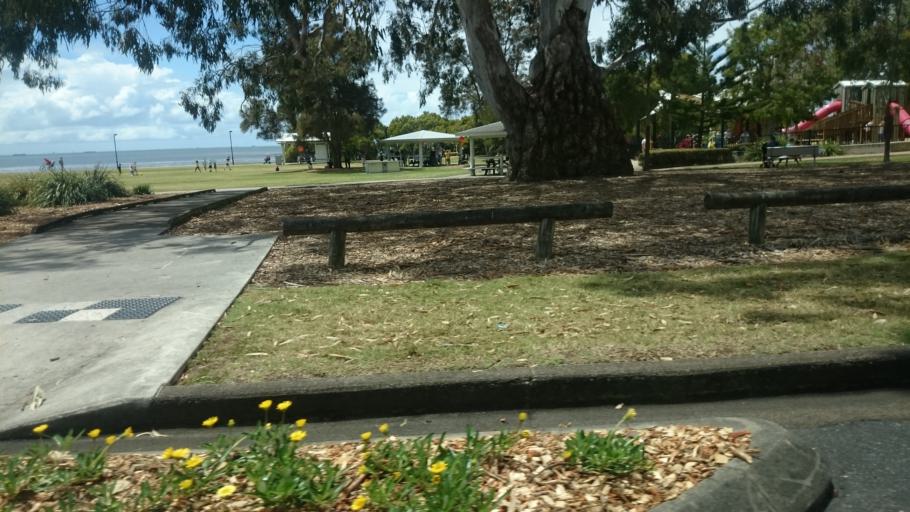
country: AU
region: Queensland
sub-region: Brisbane
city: Manly West
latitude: -27.4665
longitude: 153.1917
